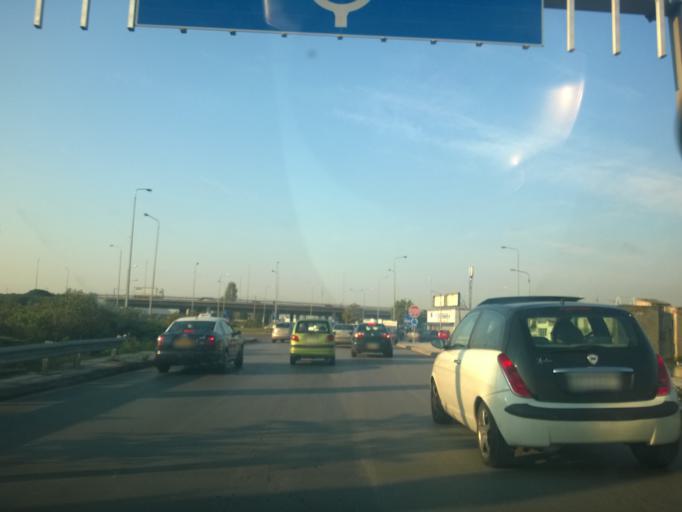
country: GR
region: Central Macedonia
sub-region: Nomos Thessalonikis
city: Menemeni
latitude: 40.6551
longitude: 22.9009
